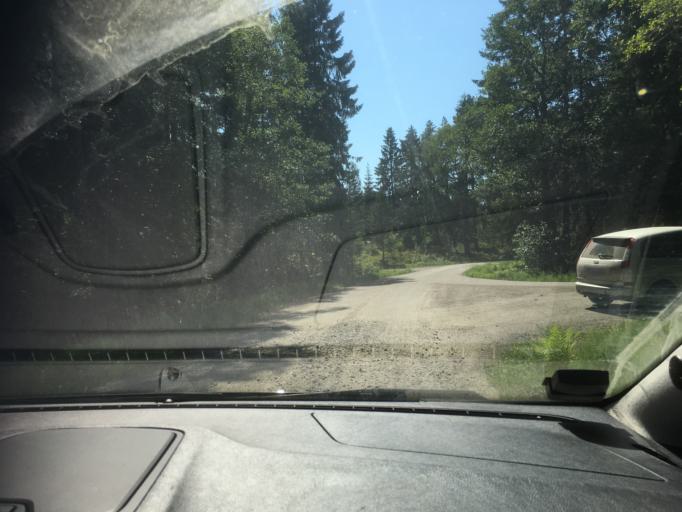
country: SE
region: Stockholm
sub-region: Haninge Kommun
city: Jordbro
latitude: 59.0122
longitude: 18.1578
